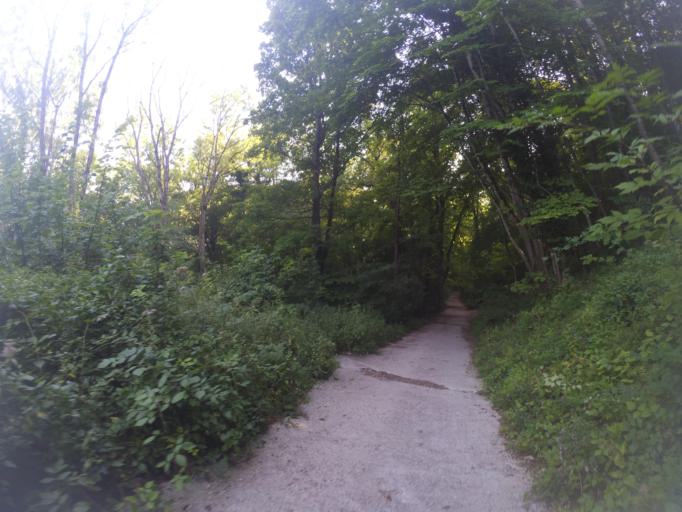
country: DE
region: Baden-Wuerttemberg
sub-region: Tuebingen Region
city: Bad Urach
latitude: 48.4930
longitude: 9.3791
